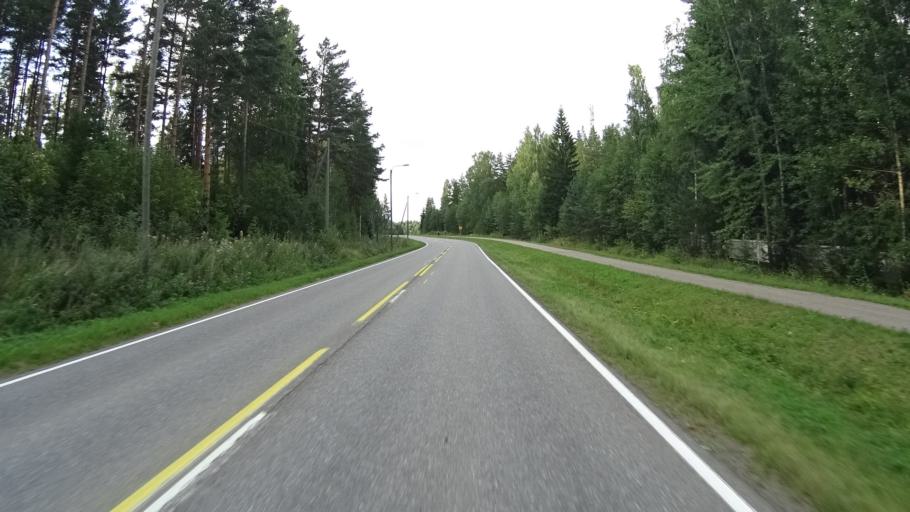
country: FI
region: Uusimaa
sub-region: Helsinki
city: Nurmijaervi
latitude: 60.3376
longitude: 24.8641
